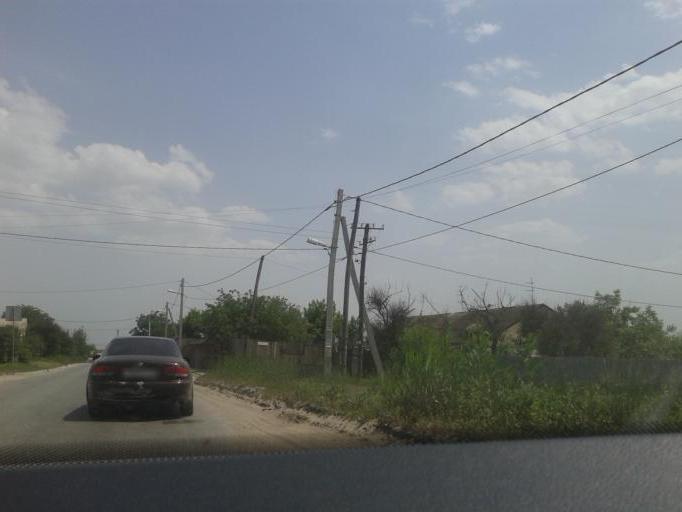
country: RU
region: Volgograd
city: Volgograd
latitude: 48.6946
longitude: 44.4485
